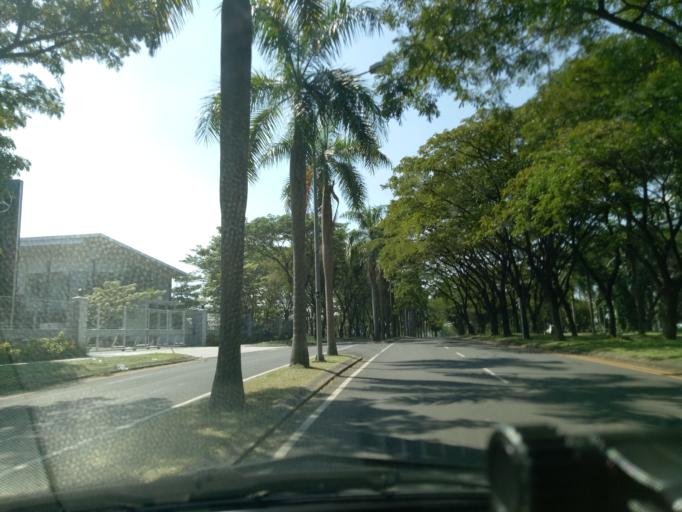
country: ID
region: East Java
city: Driyorejo
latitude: -7.2893
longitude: 112.6349
